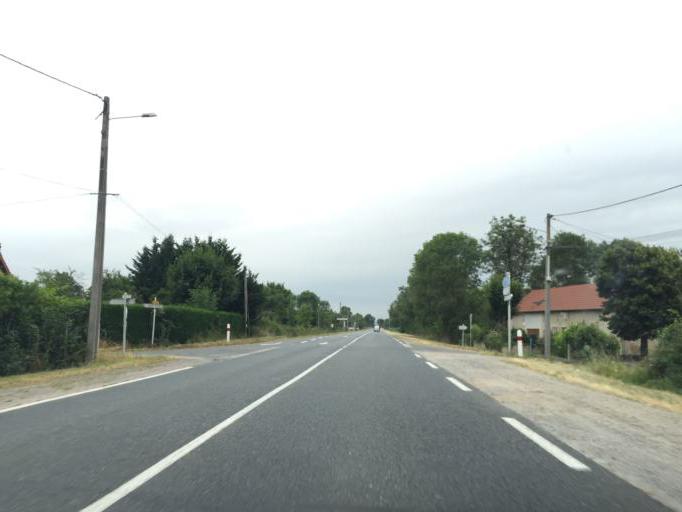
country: FR
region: Auvergne
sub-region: Departement de l'Allier
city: Brout-Vernet
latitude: 46.1893
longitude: 3.2618
